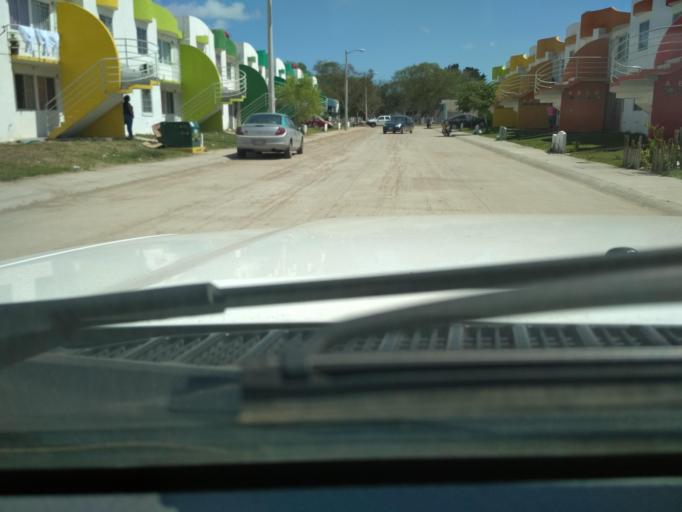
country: MX
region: Veracruz
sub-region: Veracruz
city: Las Amapolas
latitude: 19.1338
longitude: -96.2036
